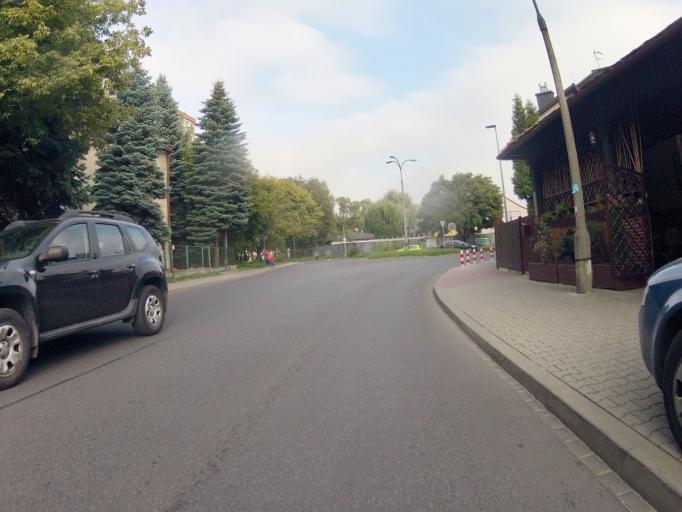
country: PL
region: Lesser Poland Voivodeship
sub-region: Krakow
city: Krakow
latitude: 50.0817
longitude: 19.9781
